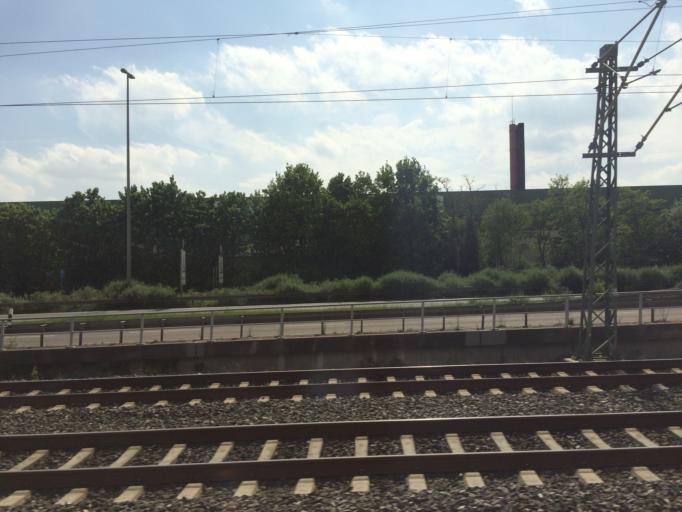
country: DE
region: Bavaria
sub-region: Regierungsbezirk Mittelfranken
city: Wetzendorf
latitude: 49.4506
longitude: 11.0417
